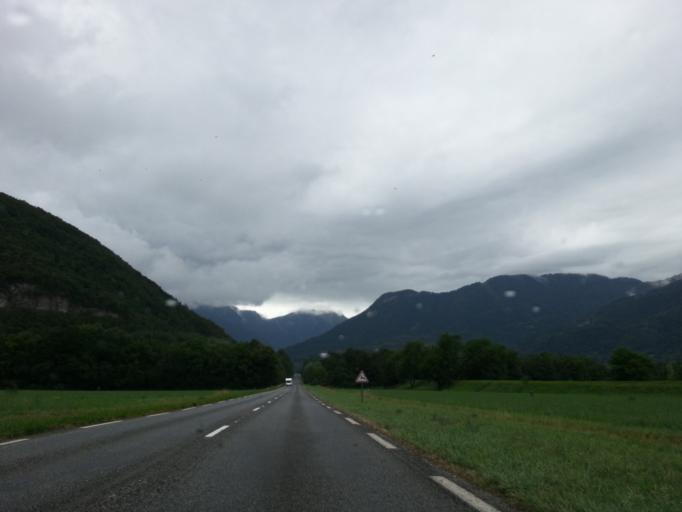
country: FR
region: Rhone-Alpes
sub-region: Departement de la Haute-Savoie
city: Doussard
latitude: 45.7751
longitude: 6.2366
